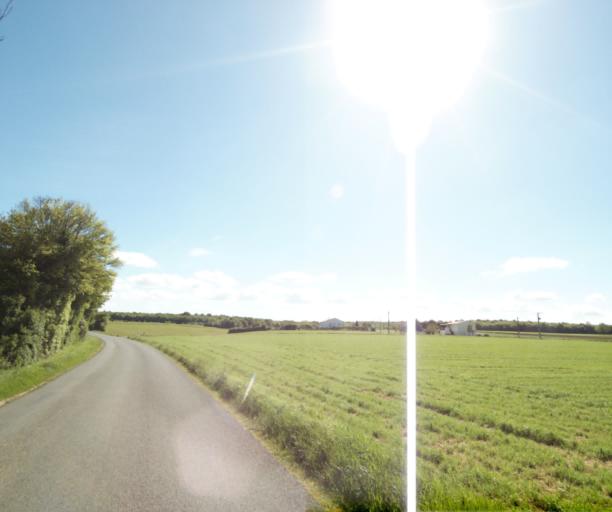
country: FR
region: Poitou-Charentes
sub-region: Departement de la Charente-Maritime
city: Bussac-sur-Charente
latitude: 45.8154
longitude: -0.6620
